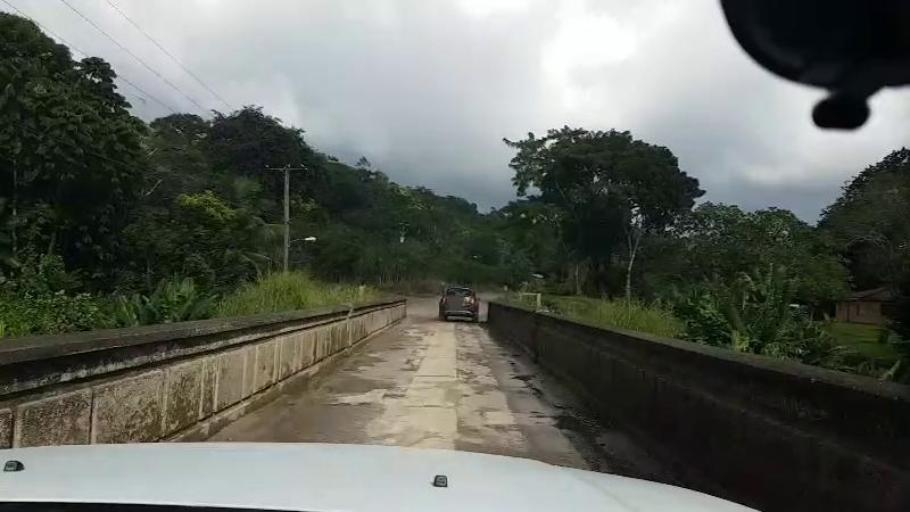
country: BZ
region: Stann Creek
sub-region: Dangriga
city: Dangriga
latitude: 17.0000
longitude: -88.4230
